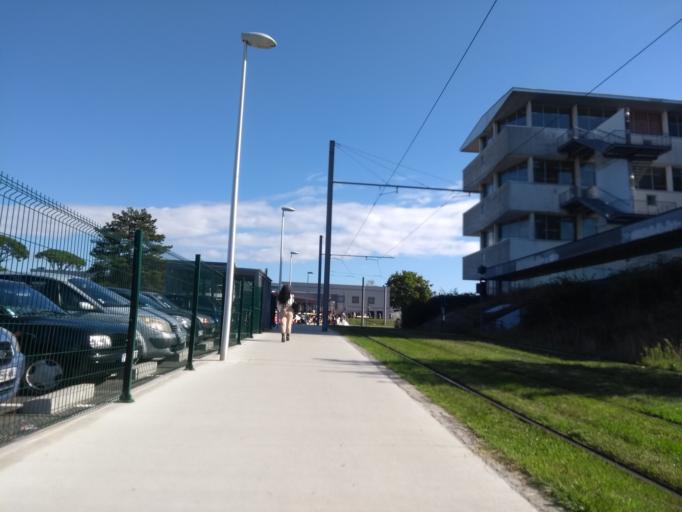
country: FR
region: Aquitaine
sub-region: Departement de la Gironde
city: Pessac
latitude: 44.7968
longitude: -0.6204
